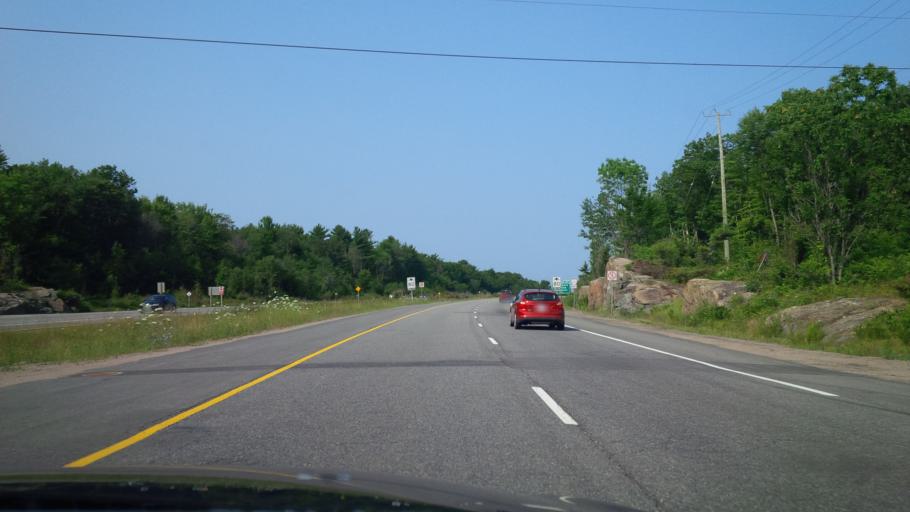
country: CA
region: Ontario
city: Gravenhurst
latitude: 44.9102
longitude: -79.3496
